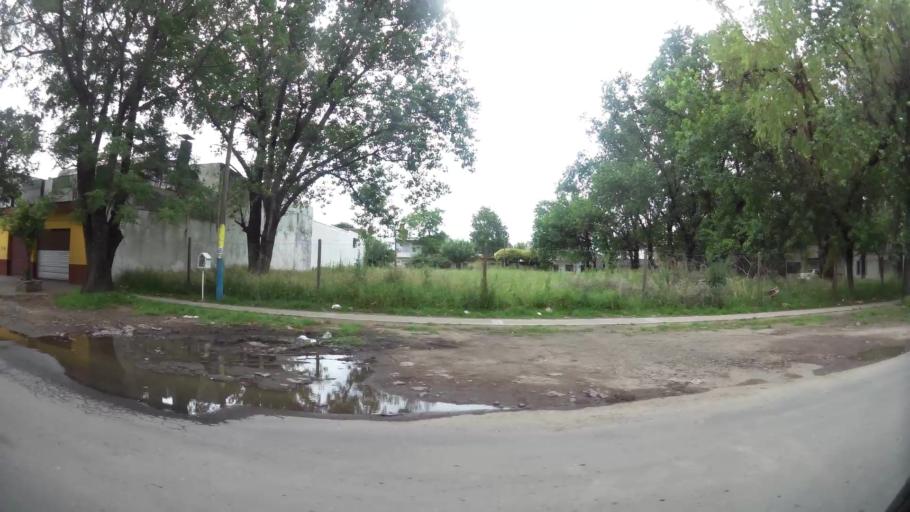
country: AR
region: Santa Fe
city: Gobernador Galvez
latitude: -32.9975
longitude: -60.6612
